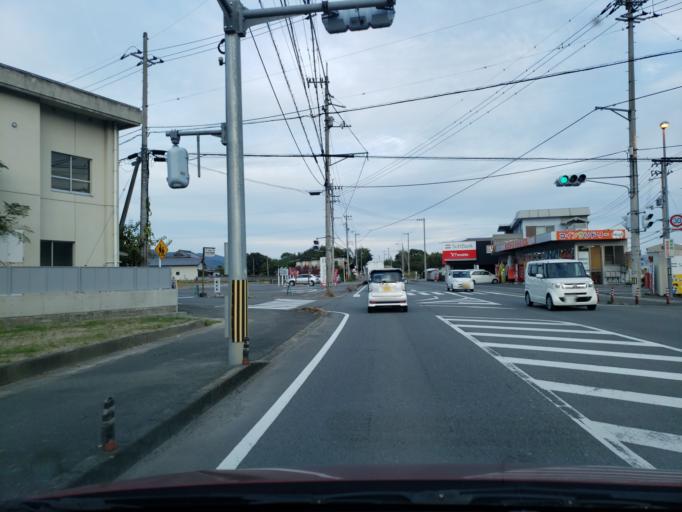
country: JP
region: Tokushima
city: Kamojimacho-jogejima
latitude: 34.0979
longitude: 134.3258
